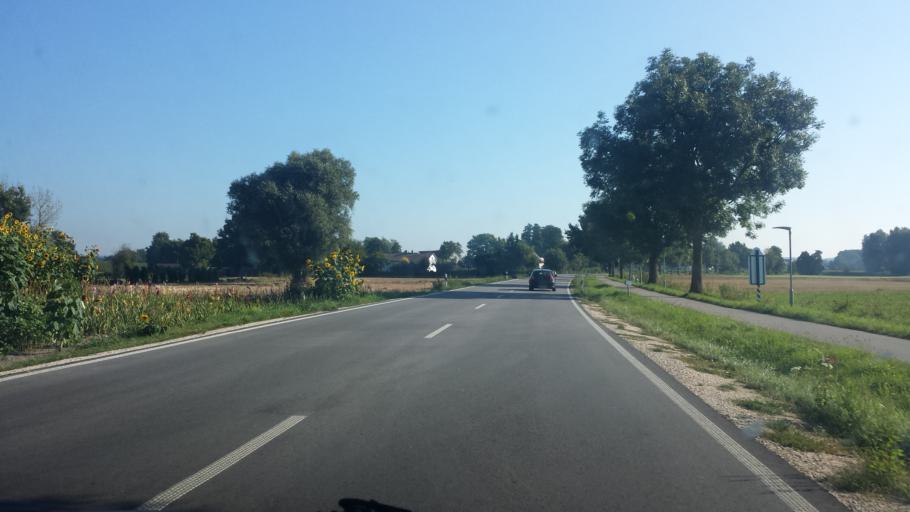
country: DE
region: Bavaria
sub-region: Lower Bavaria
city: Neustadt an der Donau
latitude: 48.8146
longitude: 11.7676
